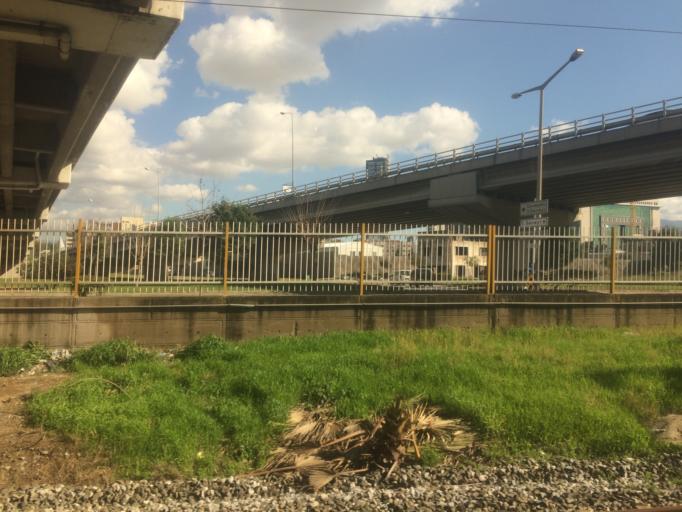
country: TR
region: Izmir
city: Buca
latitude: 38.4452
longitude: 27.1735
